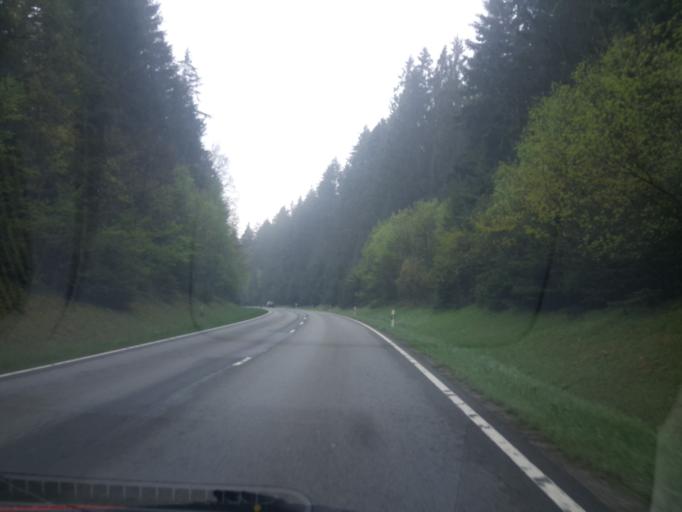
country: DE
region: Bavaria
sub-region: Lower Bavaria
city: Viechtach
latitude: 49.0479
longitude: 12.9265
